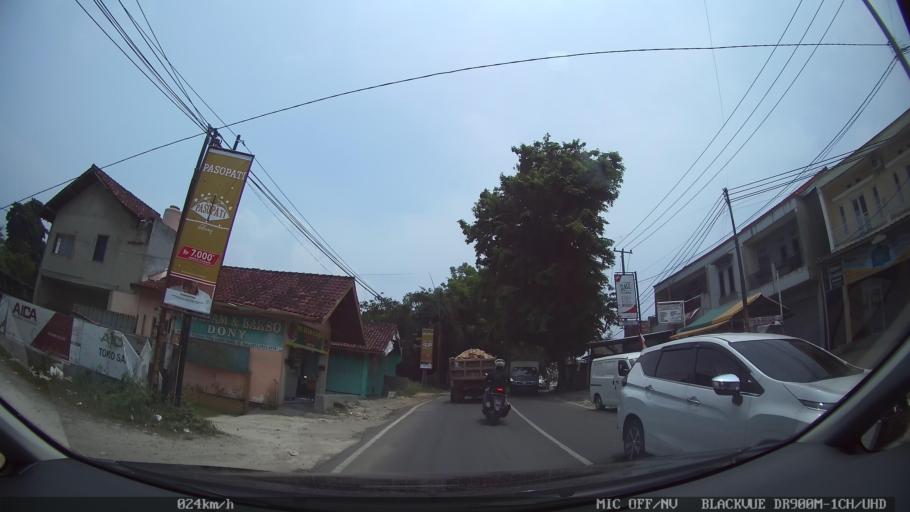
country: ID
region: Lampung
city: Bandarlampung
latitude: -5.4119
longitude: 105.2867
